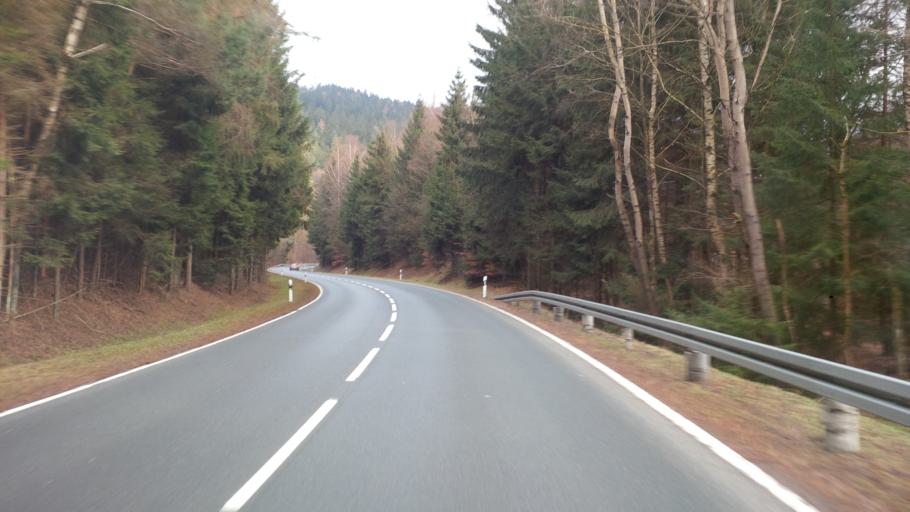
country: DE
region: Hesse
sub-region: Regierungsbezirk Darmstadt
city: Schmitten
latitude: 50.2309
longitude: 8.4923
